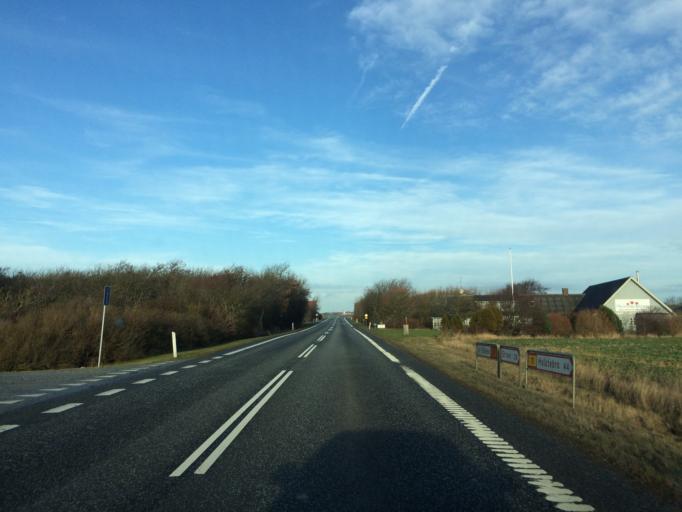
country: DK
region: North Denmark
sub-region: Thisted Kommune
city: Hurup
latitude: 56.6920
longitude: 8.4020
